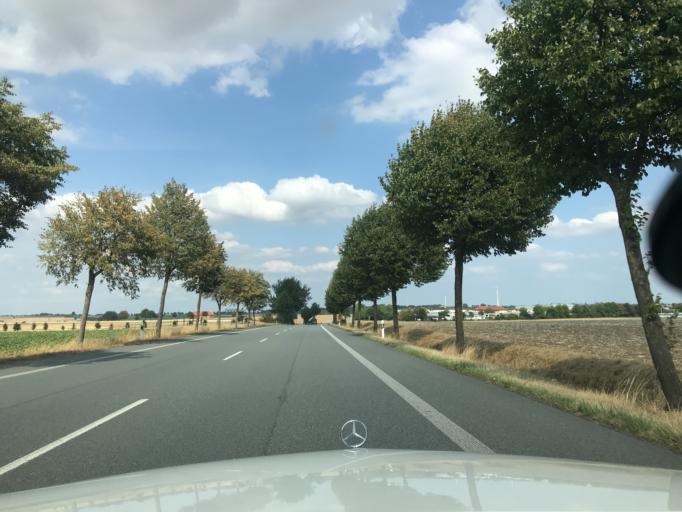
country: DE
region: North Rhine-Westphalia
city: Warburg
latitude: 51.4995
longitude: 9.1232
